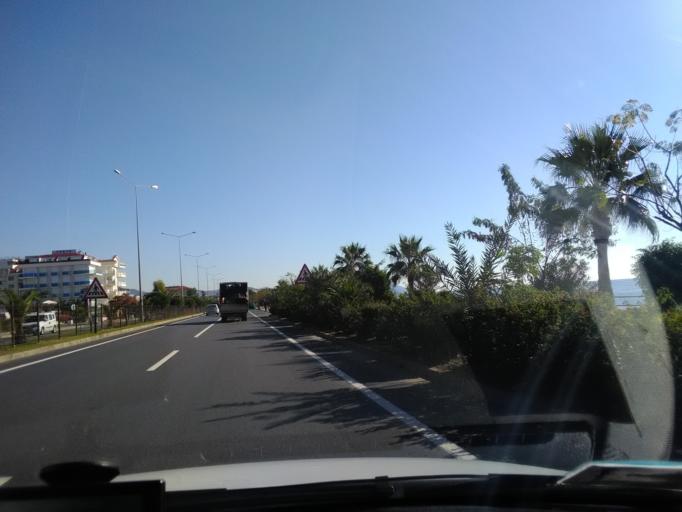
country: TR
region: Antalya
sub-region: Alanya
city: Mahmutlar
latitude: 36.5098
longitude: 32.0699
